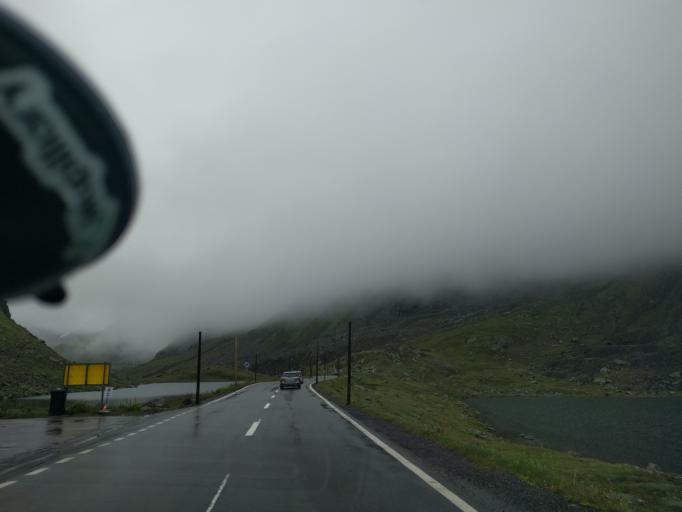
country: CH
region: Grisons
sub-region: Praettigau/Davos District
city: Davos
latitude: 46.7501
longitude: 9.9477
